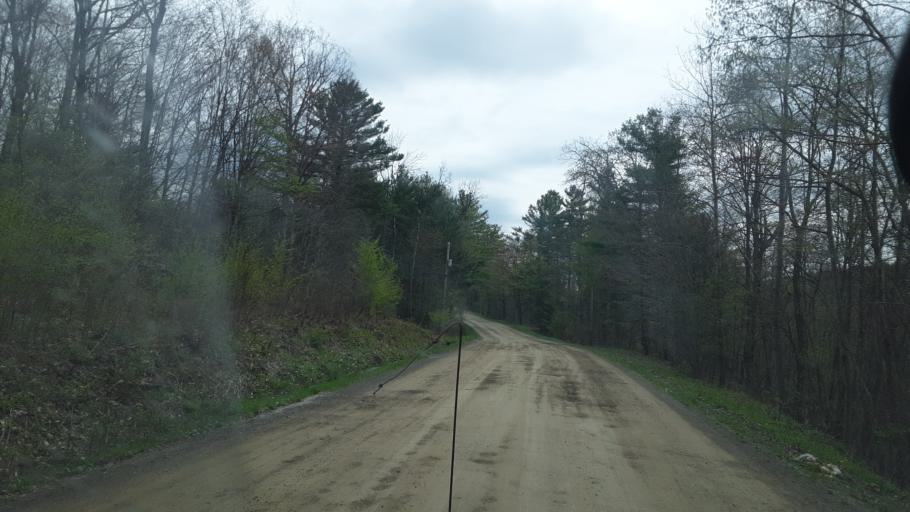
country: US
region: New York
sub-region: Steuben County
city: Addison
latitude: 42.0960
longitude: -77.3293
